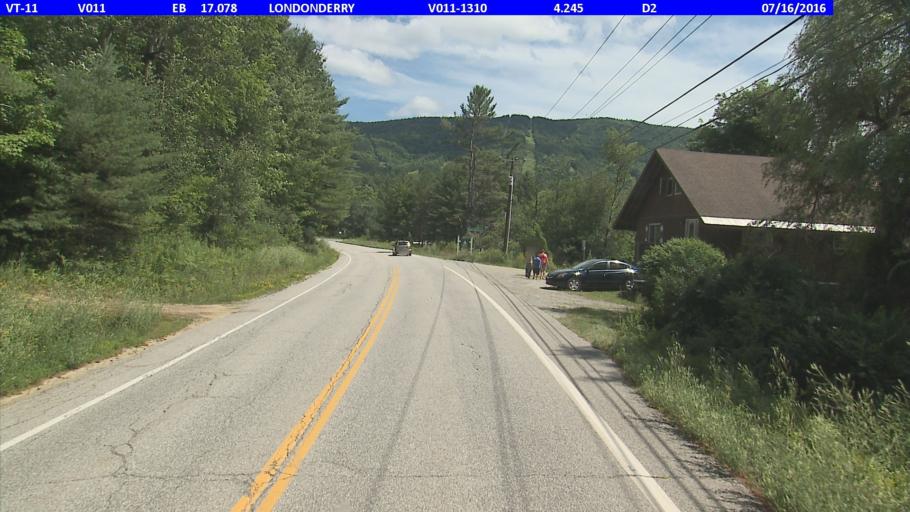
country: US
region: Vermont
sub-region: Windsor County
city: Chester
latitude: 43.2088
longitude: -72.7825
